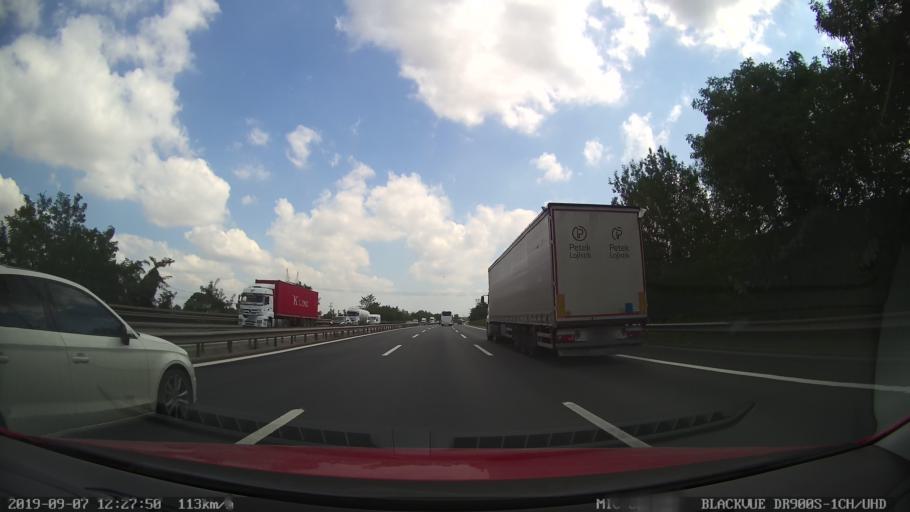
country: TR
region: Sakarya
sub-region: Merkez
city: Sapanca
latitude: 40.7118
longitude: 30.3308
